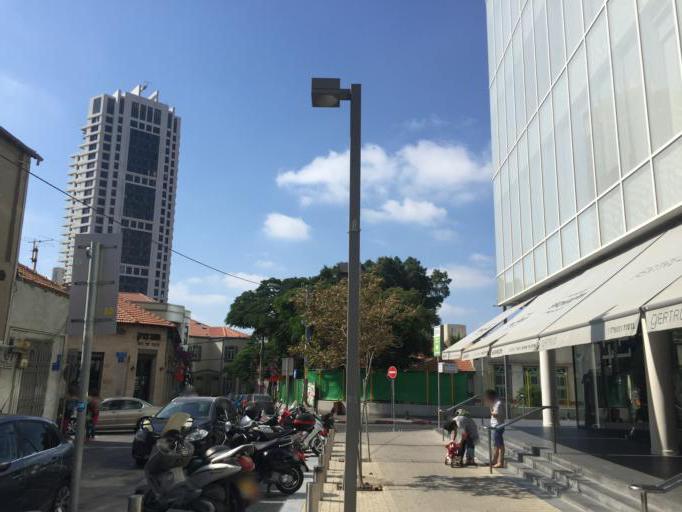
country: IL
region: Tel Aviv
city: Yafo
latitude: 32.0632
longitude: 34.7687
